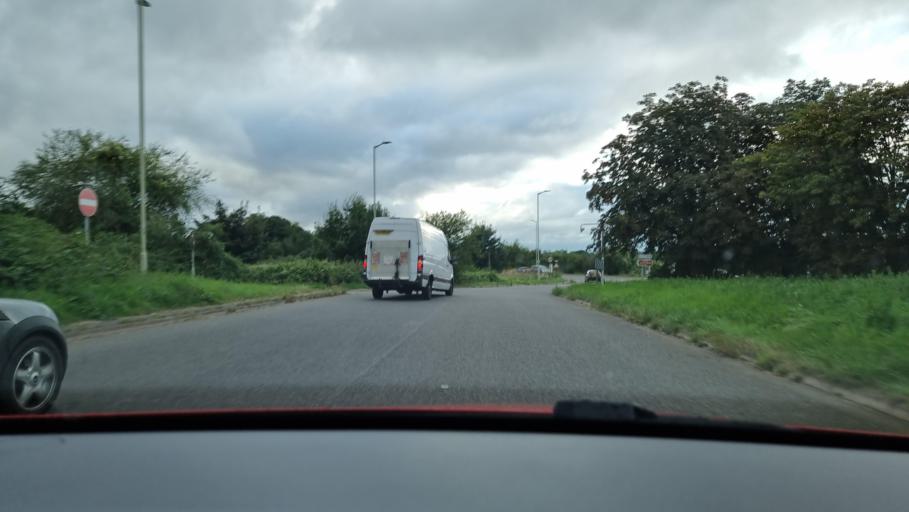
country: GB
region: England
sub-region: Hertfordshire
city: Tring
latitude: 51.7909
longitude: -0.6447
